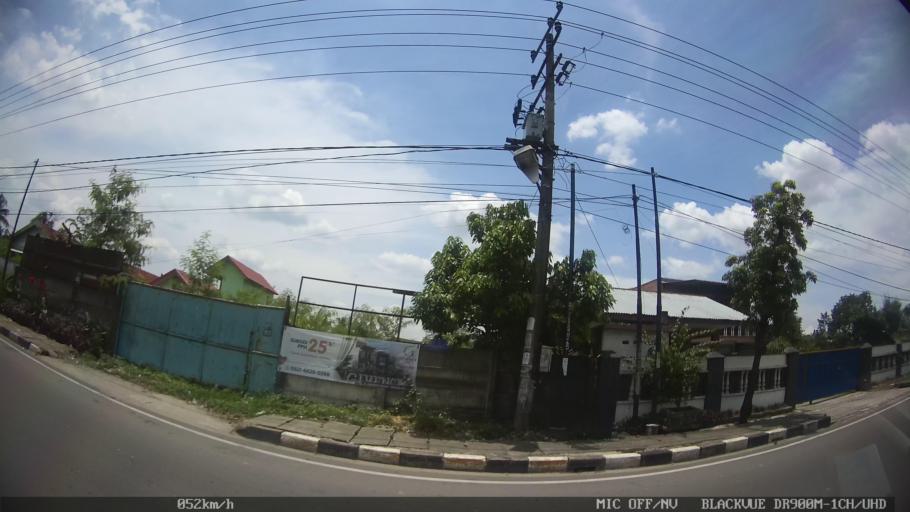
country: ID
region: North Sumatra
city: Binjai
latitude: 3.6060
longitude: 98.5292
